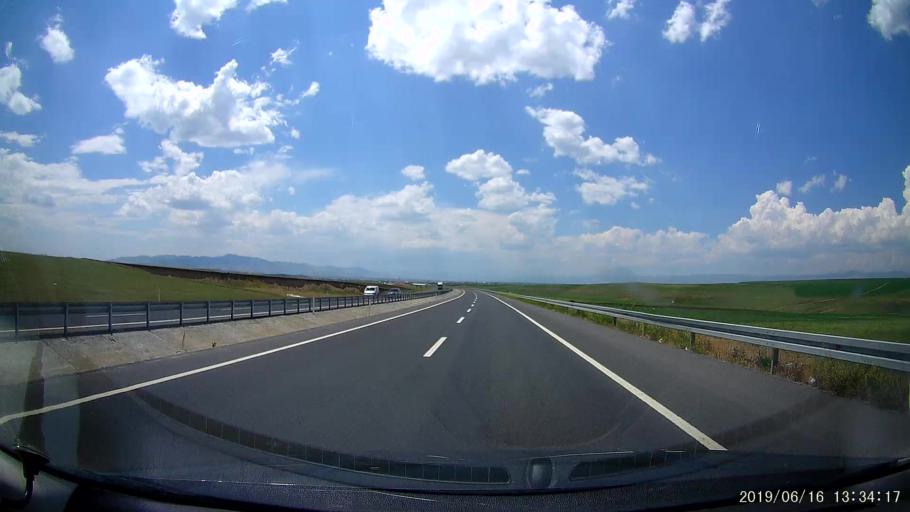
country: TR
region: Agri
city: Agri
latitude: 39.7123
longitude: 43.1309
